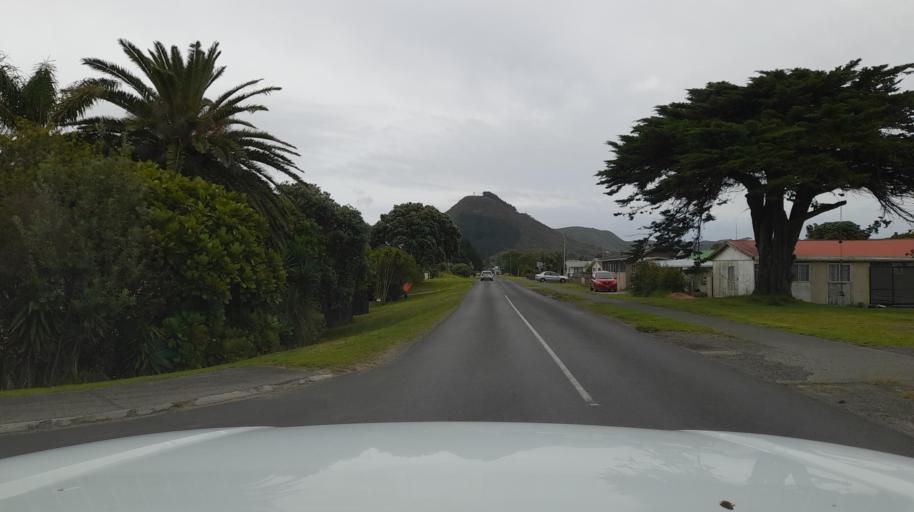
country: NZ
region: Northland
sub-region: Far North District
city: Ahipara
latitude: -35.1632
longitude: 173.1581
